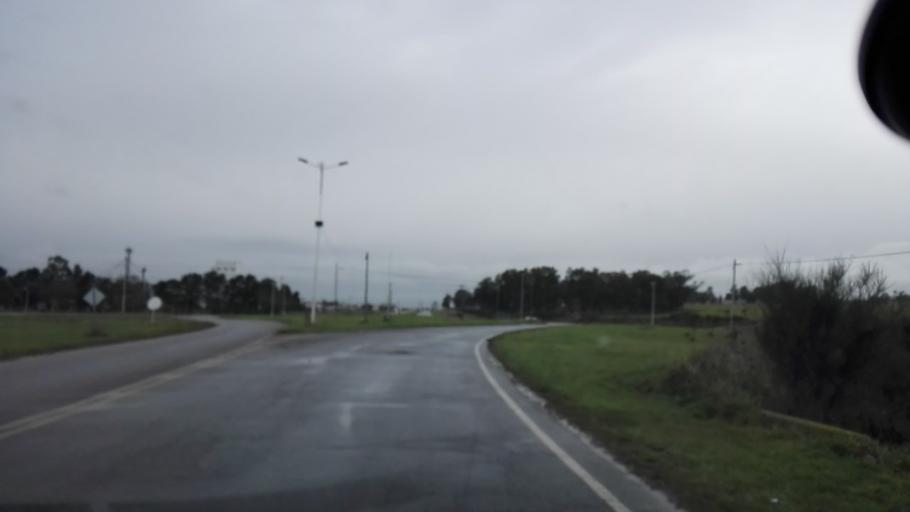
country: AR
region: Buenos Aires
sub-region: Partido de Tandil
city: Tandil
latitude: -37.2985
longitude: -59.1846
